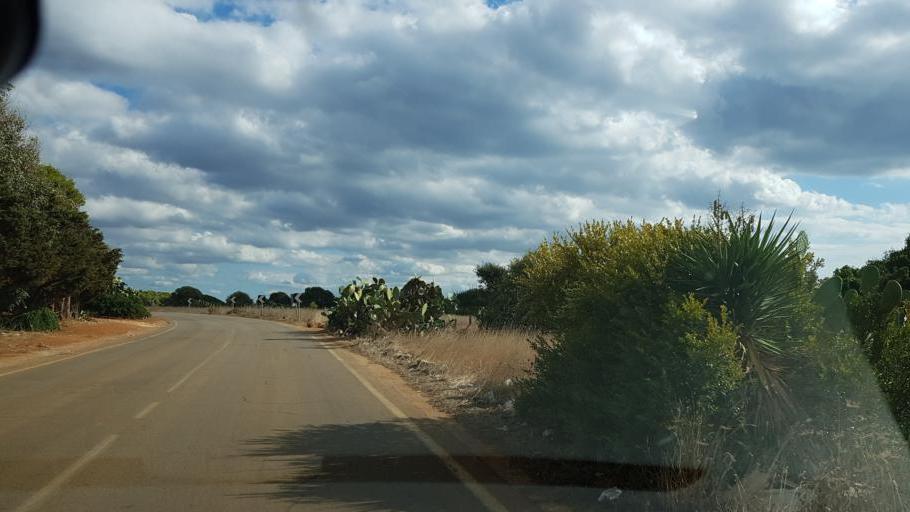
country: IT
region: Apulia
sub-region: Provincia di Lecce
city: Nardo
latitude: 40.1605
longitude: 17.9552
